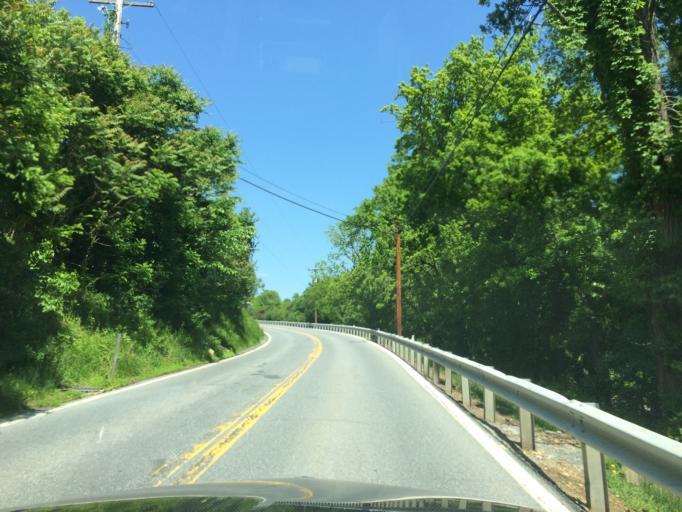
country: US
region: Maryland
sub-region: Frederick County
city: Myersville
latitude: 39.4813
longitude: -77.5420
